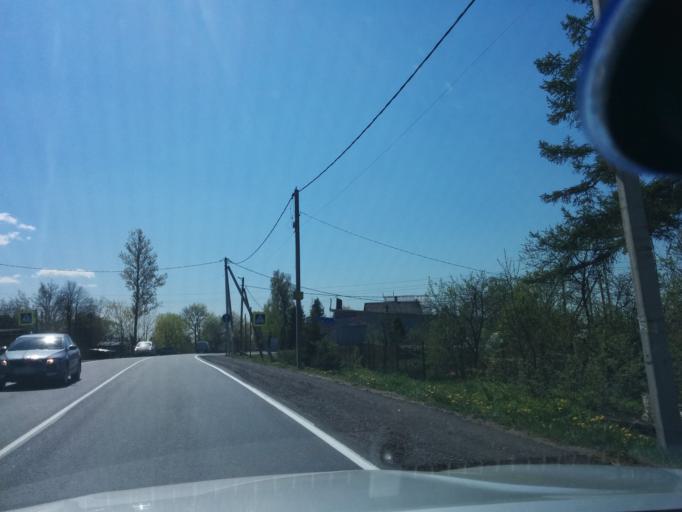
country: RU
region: Leningrad
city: Verkhniye Osel'ki
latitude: 60.2221
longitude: 30.4339
